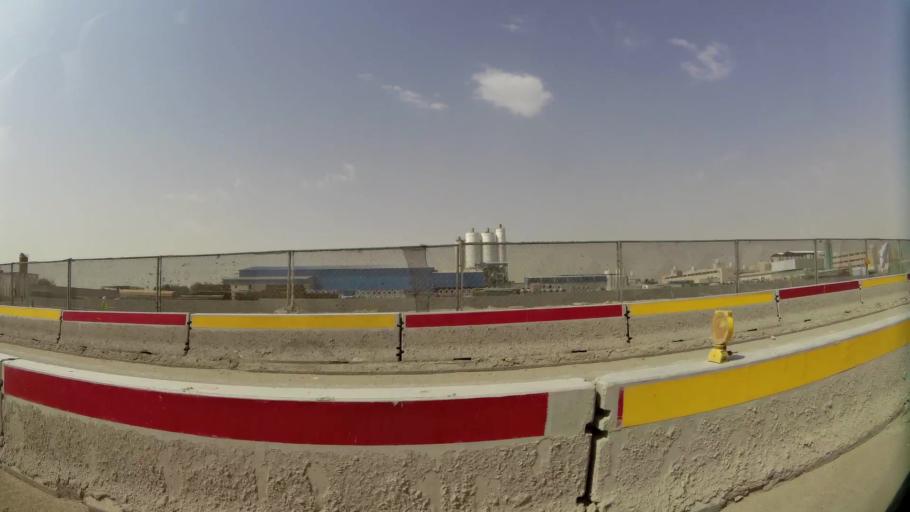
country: QA
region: Al Wakrah
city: Al Wukayr
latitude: 25.1658
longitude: 51.4534
